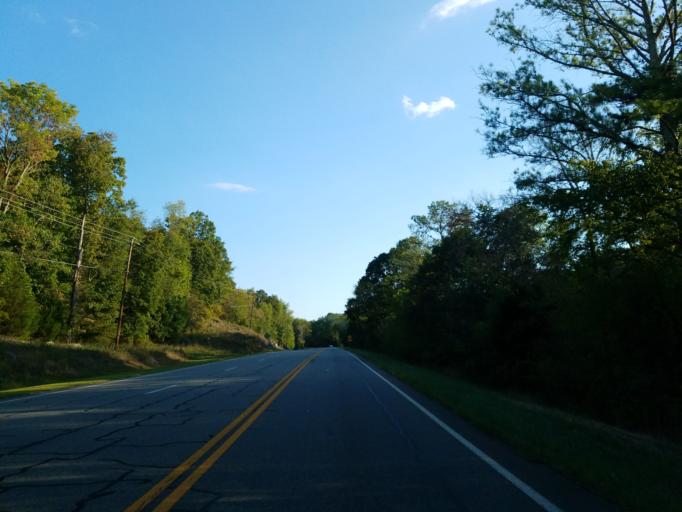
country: US
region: Georgia
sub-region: Bartow County
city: Rydal
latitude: 34.5471
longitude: -84.7073
